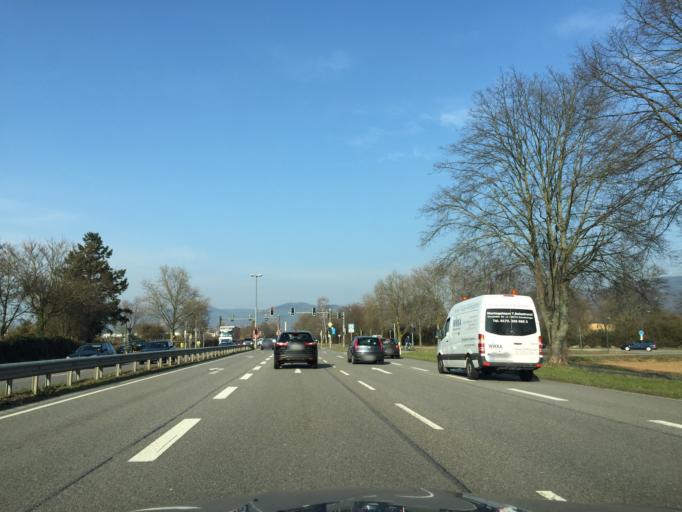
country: DE
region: Baden-Wuerttemberg
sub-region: Karlsruhe Region
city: Eppelheim
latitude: 49.3880
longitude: 8.6606
